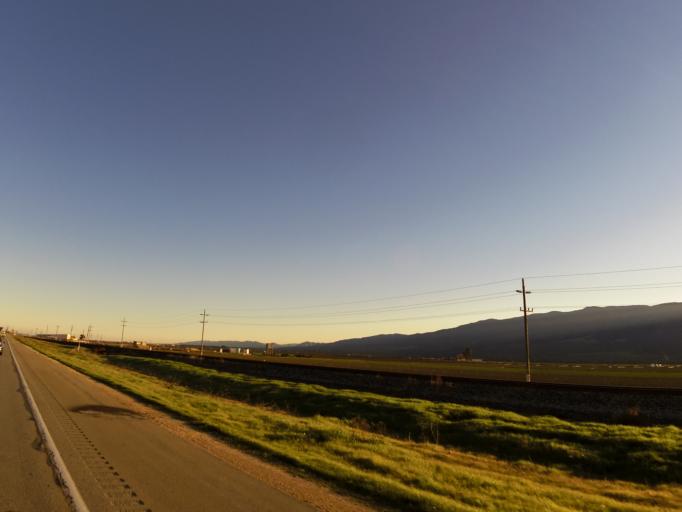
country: US
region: California
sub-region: Monterey County
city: Gonzales
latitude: 36.4721
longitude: -121.4001
